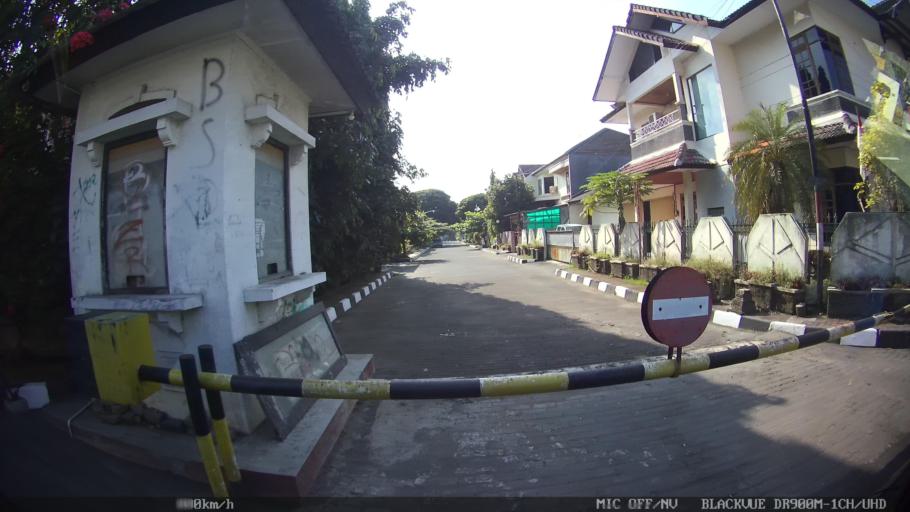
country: ID
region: Daerah Istimewa Yogyakarta
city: Depok
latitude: -7.7633
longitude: 110.3975
